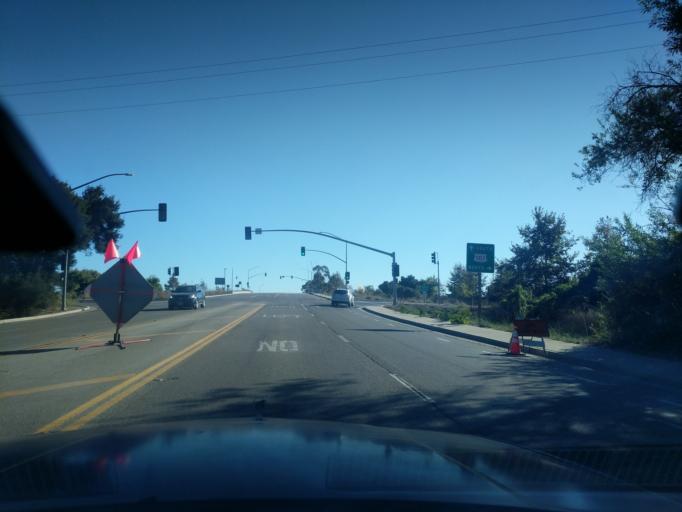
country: US
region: California
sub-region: Santa Barbara County
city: Goleta
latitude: 34.4392
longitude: -119.8530
